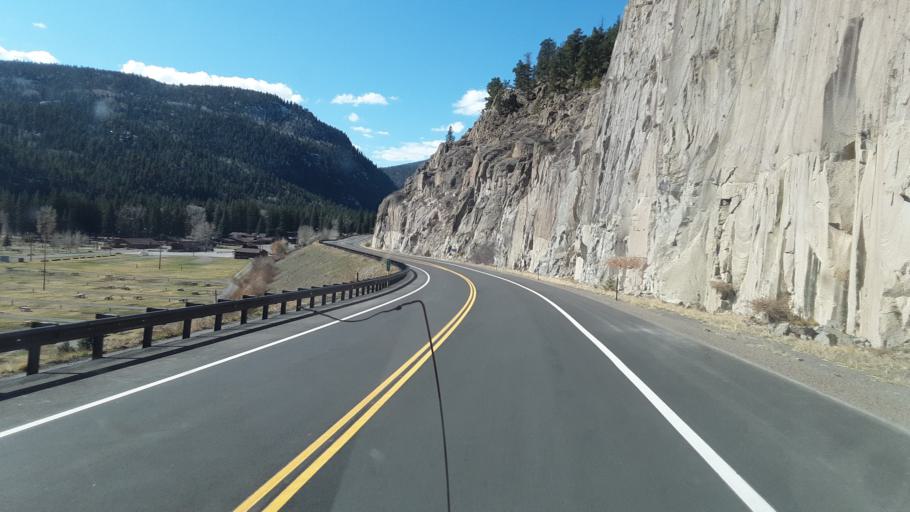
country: US
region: Colorado
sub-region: Mineral County
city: Creede
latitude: 37.6150
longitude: -106.6977
